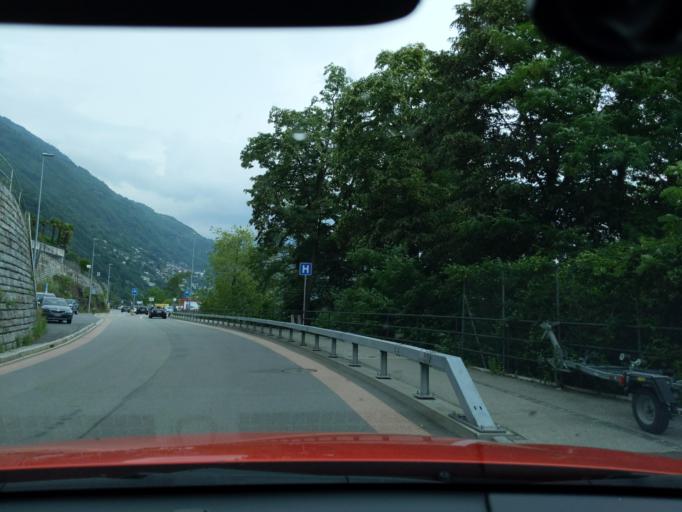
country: CH
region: Ticino
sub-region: Locarno District
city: Brissago
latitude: 46.1238
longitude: 8.7147
